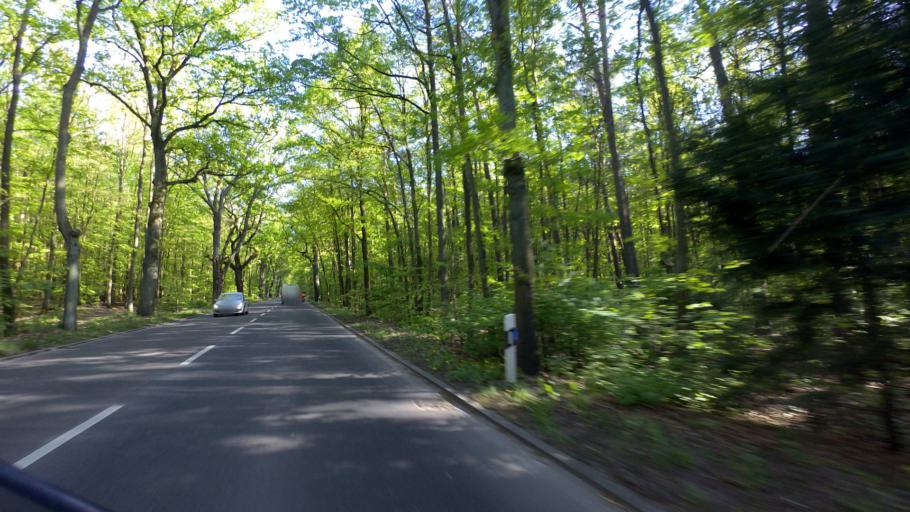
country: DE
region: Brandenburg
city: Hohen Neuendorf
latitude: 52.6587
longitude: 13.2883
